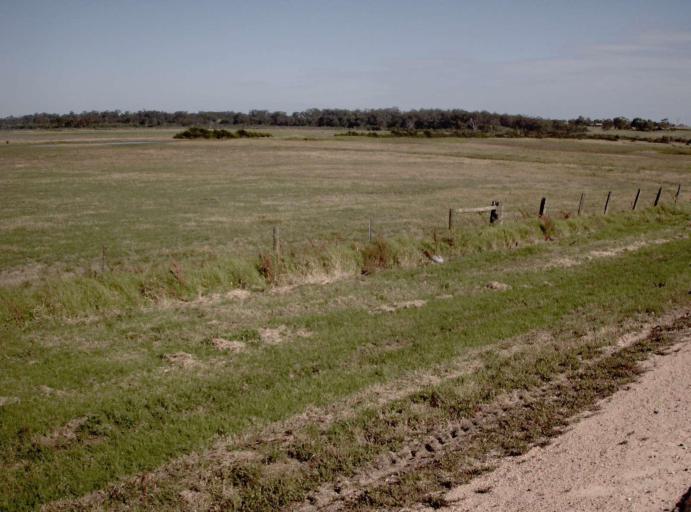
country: AU
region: Victoria
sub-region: East Gippsland
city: Lakes Entrance
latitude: -37.7704
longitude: 148.5368
